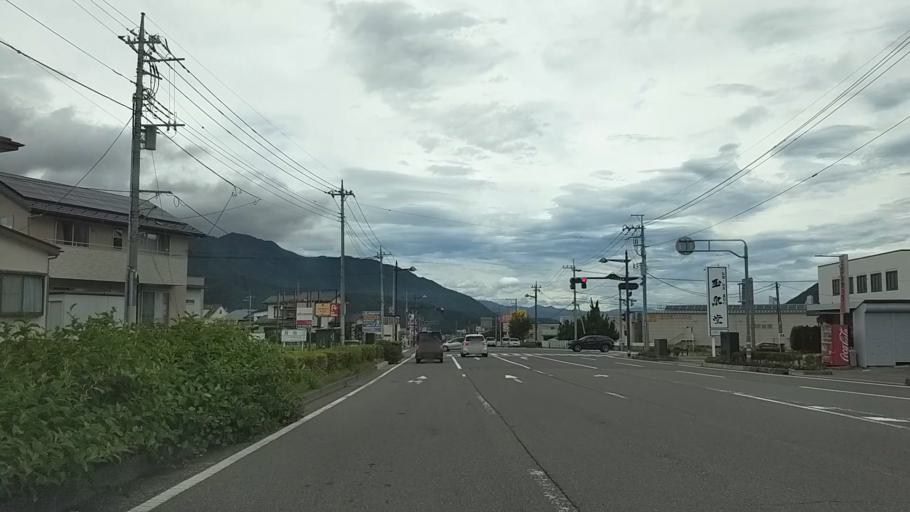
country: JP
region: Yamanashi
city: Fujikawaguchiko
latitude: 35.4769
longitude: 138.8085
